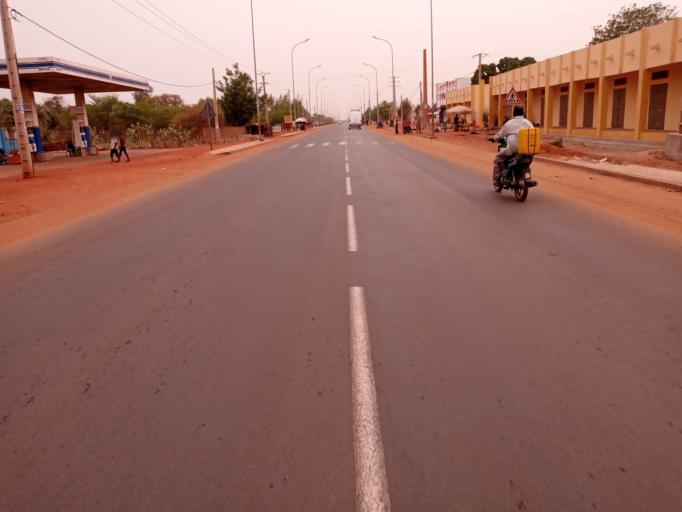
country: ML
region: Koulikoro
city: Koulikoro
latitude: 12.8431
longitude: -7.5855
